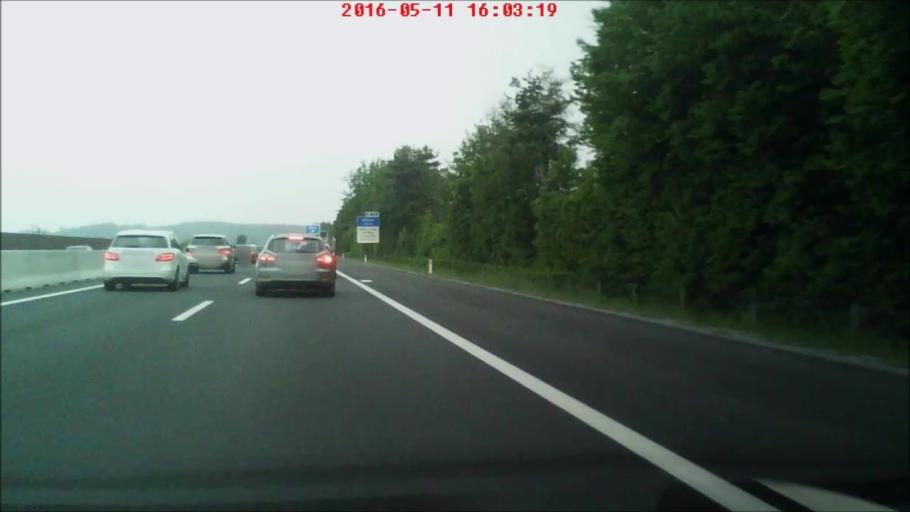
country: AT
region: Styria
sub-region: Politischer Bezirk Leibnitz
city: Weitendorf
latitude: 46.9012
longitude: 15.4722
